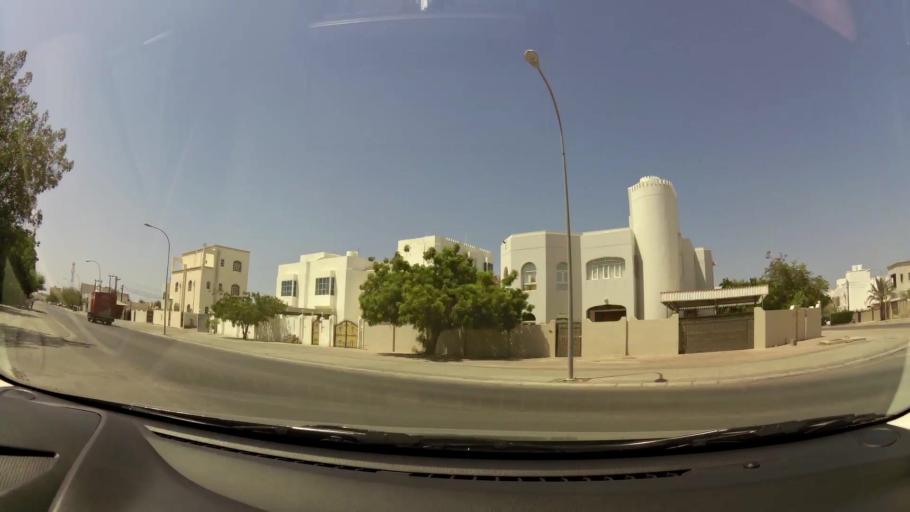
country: OM
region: Muhafazat Masqat
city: As Sib al Jadidah
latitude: 23.6224
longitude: 58.2248
